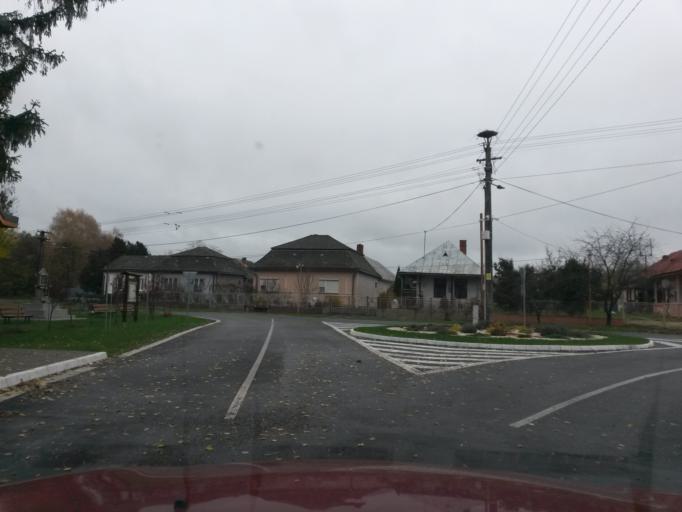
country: SK
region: Kosicky
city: Cierna nad Tisou
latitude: 48.5559
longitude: 21.9533
